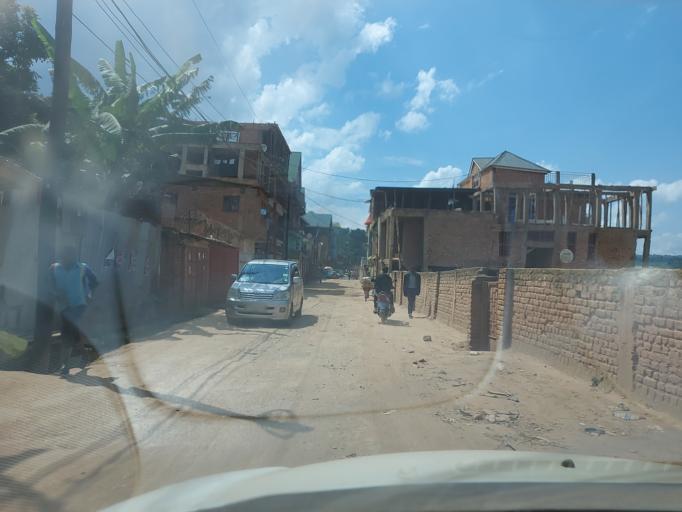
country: CD
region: South Kivu
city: Bukavu
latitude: -2.5013
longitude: 28.8738
